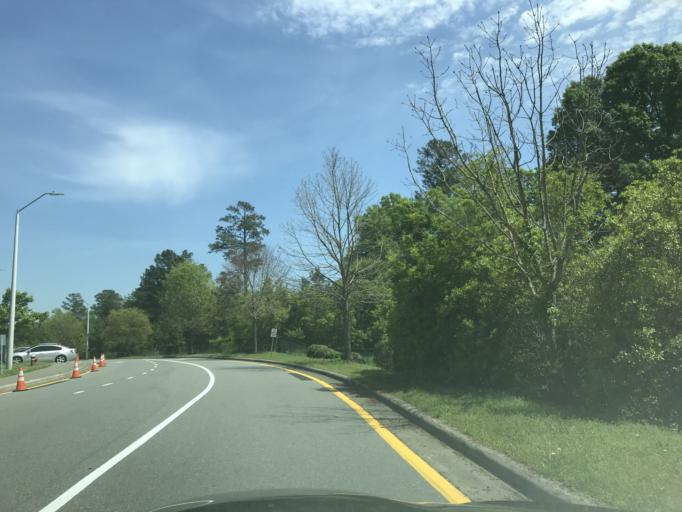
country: US
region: North Carolina
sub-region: Wake County
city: Knightdale
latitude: 35.8641
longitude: -78.5369
